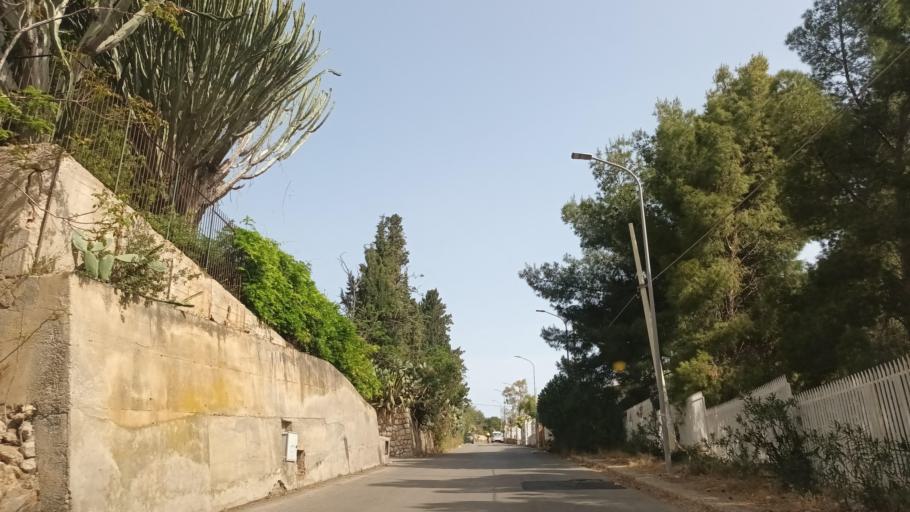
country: IT
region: Sicily
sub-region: Palermo
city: Santa Flavia
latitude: 38.1028
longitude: 13.5332
